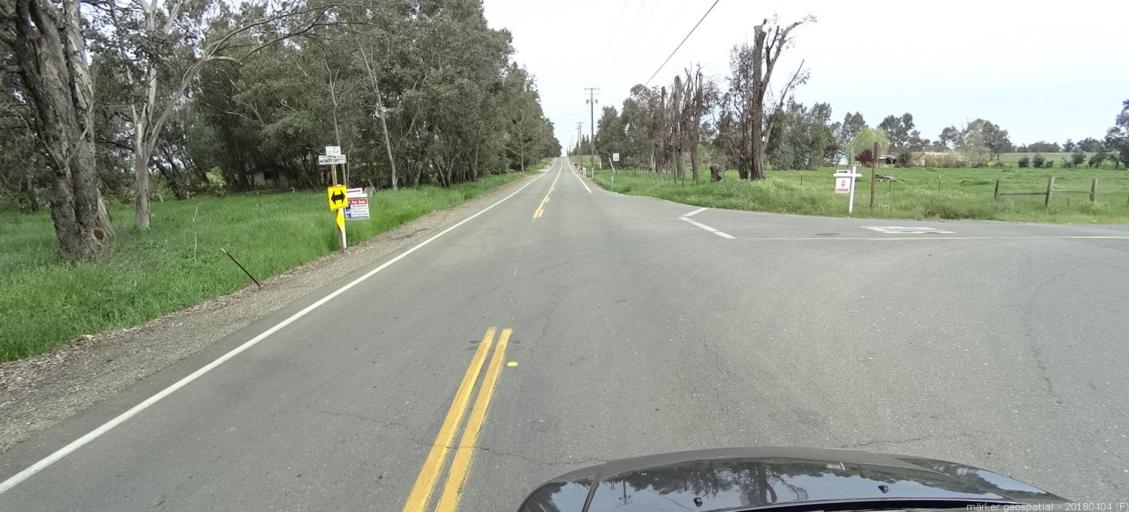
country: US
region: California
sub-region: Sacramento County
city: Clay
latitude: 38.3139
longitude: -121.1712
